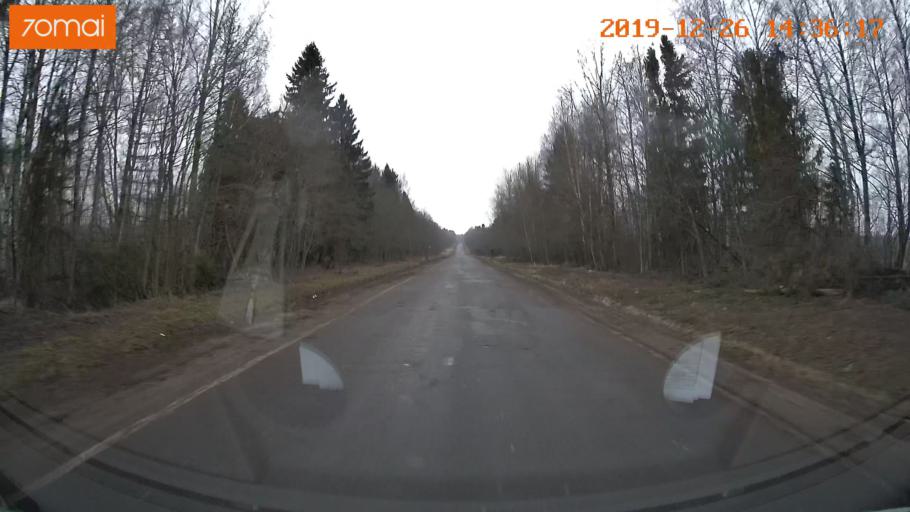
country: RU
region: Jaroslavl
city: Poshekhon'ye
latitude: 58.4128
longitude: 38.9767
